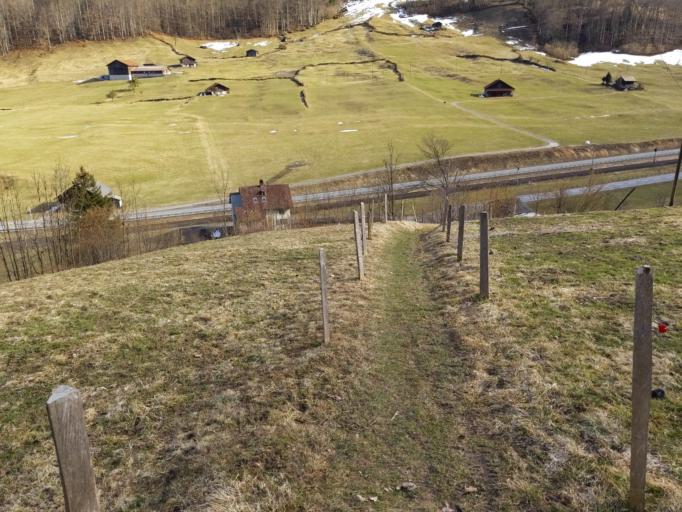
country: CH
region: Glarus
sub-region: Glarus
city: Luchsingen
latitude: 46.9446
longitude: 9.0206
